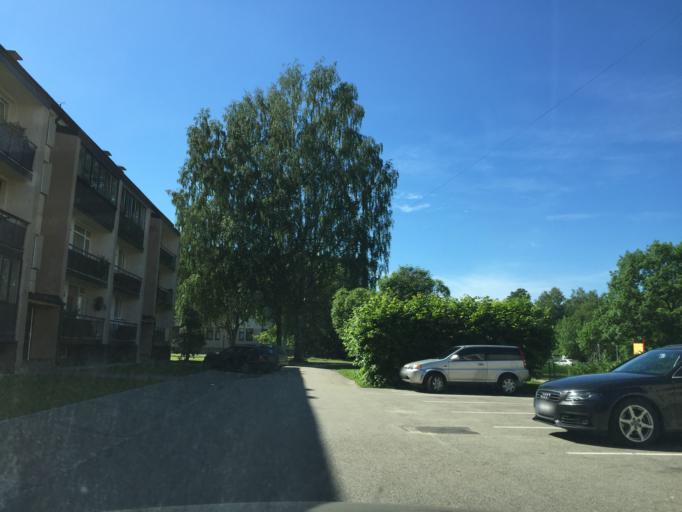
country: LV
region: Babite
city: Pinki
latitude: 56.9557
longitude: 23.9548
